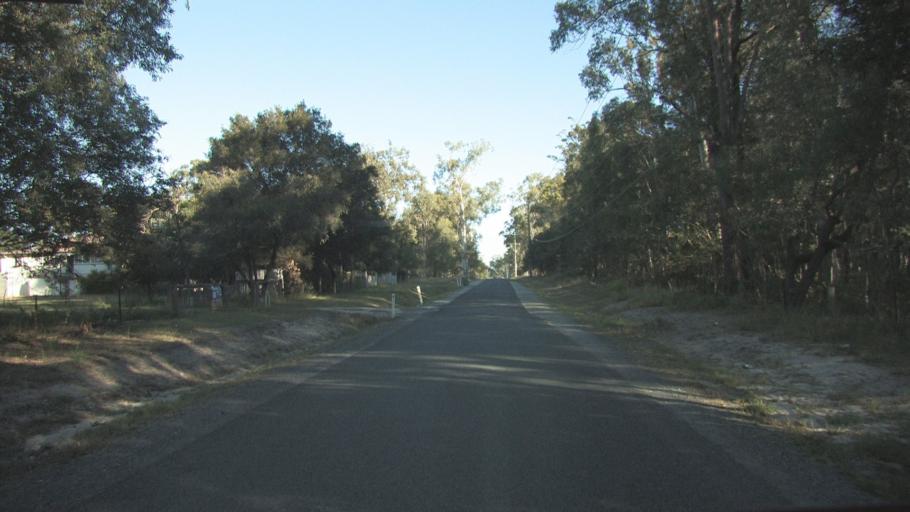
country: AU
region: Queensland
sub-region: Logan
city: Chambers Flat
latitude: -27.7856
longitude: 153.0864
